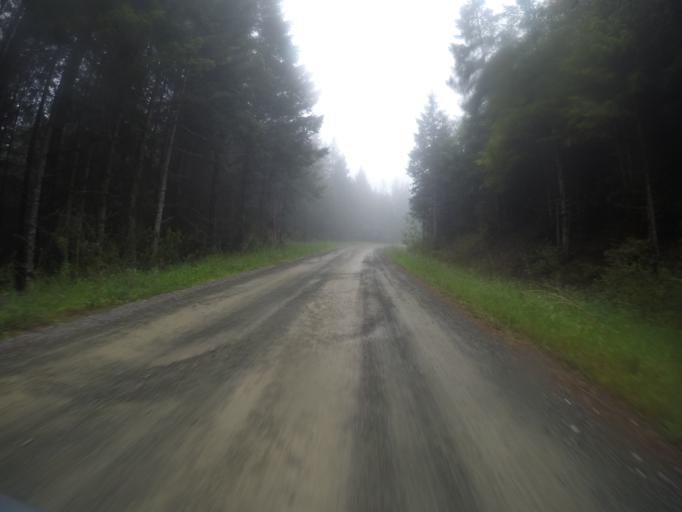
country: US
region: California
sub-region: Humboldt County
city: Westhaven-Moonstone
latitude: 41.2370
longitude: -123.9962
